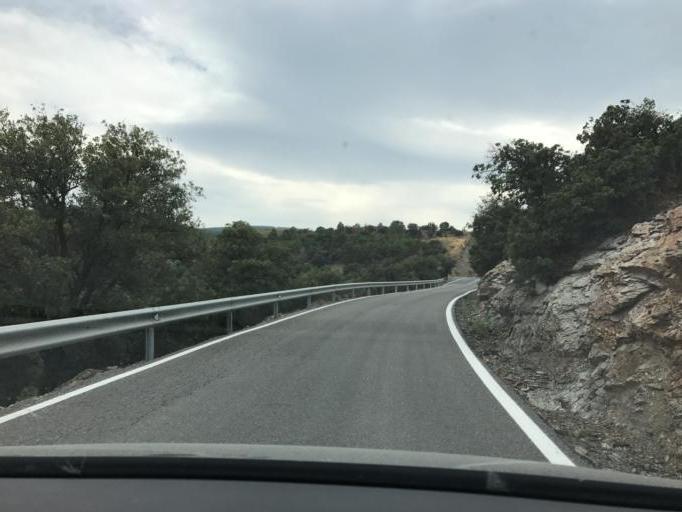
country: ES
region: Andalusia
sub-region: Provincia de Granada
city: Aldeire
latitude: 37.1536
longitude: -3.0494
